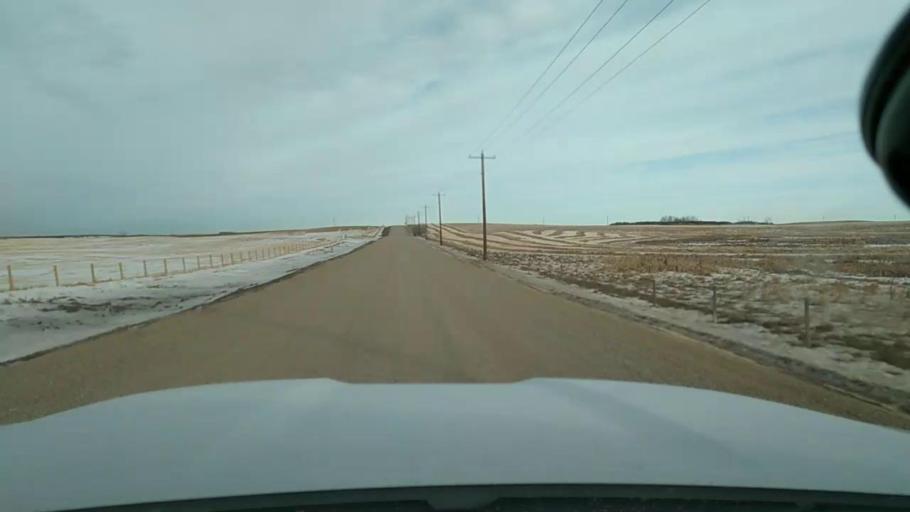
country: CA
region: Alberta
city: Airdrie
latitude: 51.2343
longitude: -113.9118
